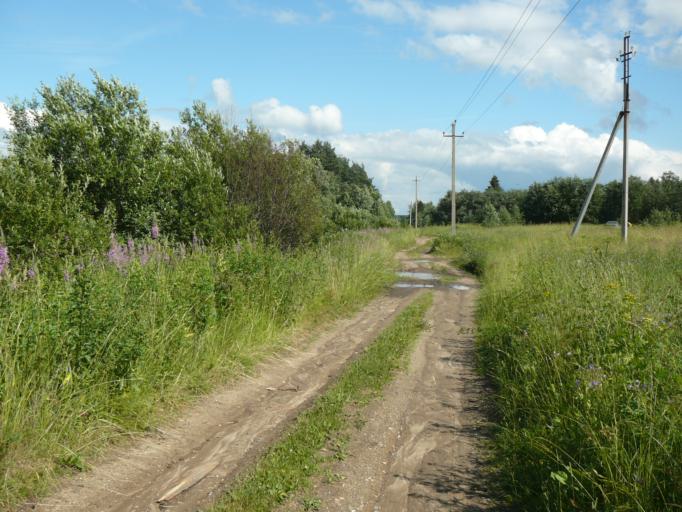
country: RU
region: Vologda
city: Kharovsk
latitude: 59.9528
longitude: 40.2543
